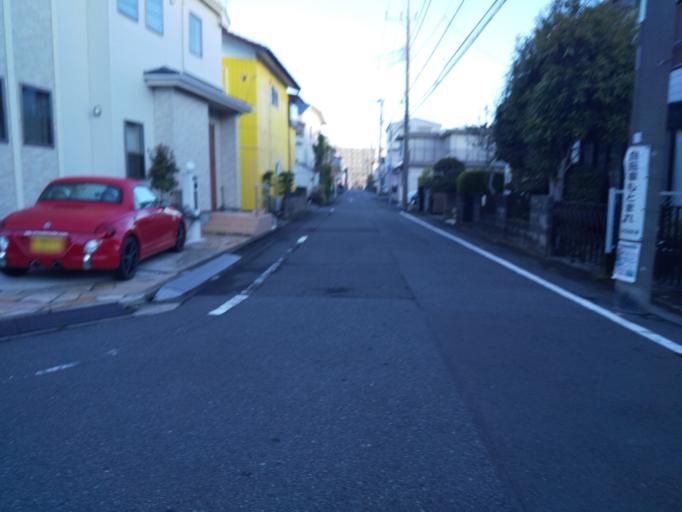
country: JP
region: Tokyo
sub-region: Machida-shi
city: Machida
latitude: 35.5629
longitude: 139.3810
